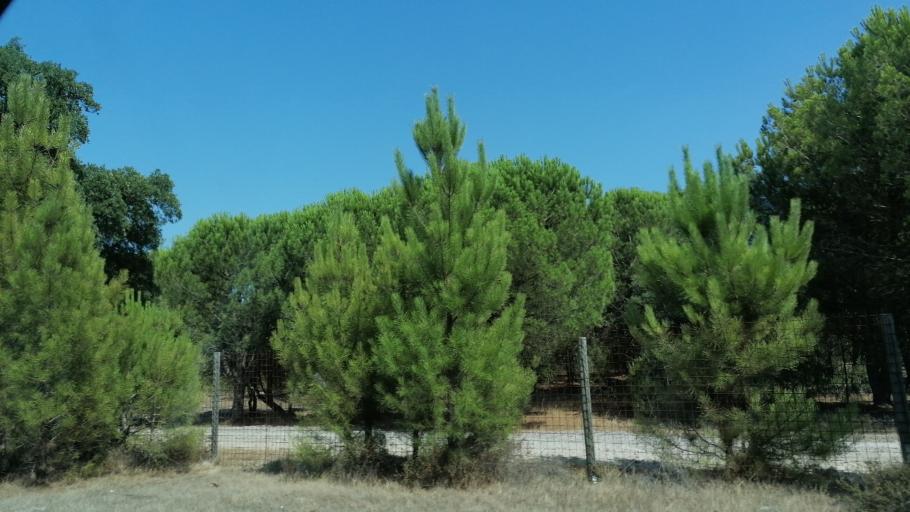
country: PT
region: Santarem
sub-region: Benavente
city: Poceirao
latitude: 38.7236
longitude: -8.7068
